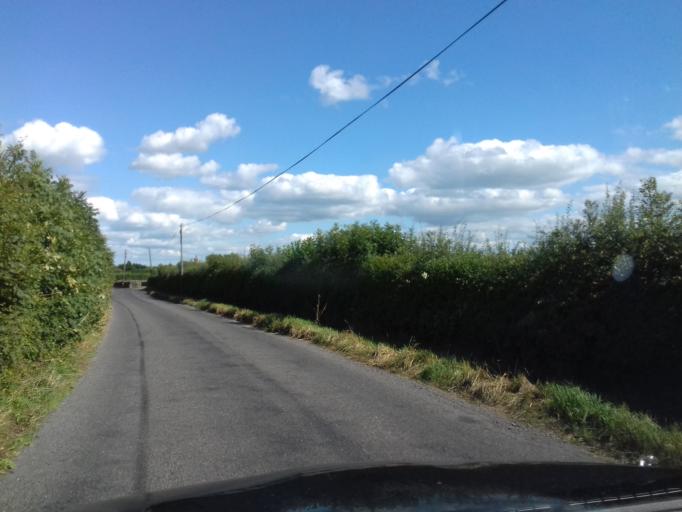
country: IE
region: Leinster
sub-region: Kilkenny
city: Callan
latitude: 52.5383
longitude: -7.3078
